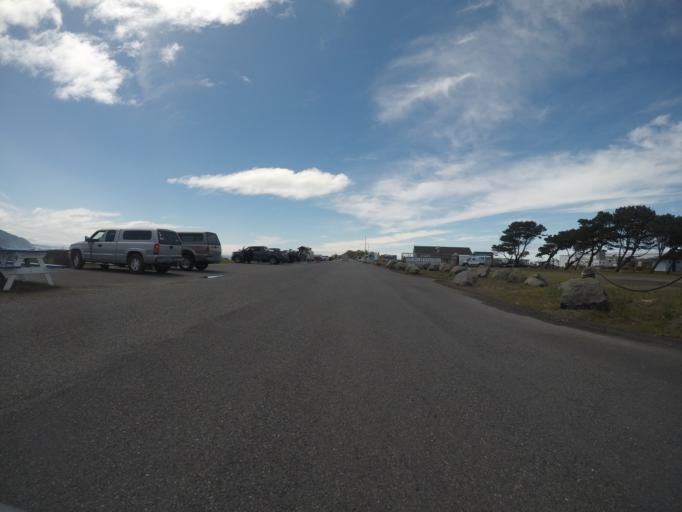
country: US
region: California
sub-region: Del Norte County
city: Bertsch-Oceanview
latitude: 41.7454
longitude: -124.1791
